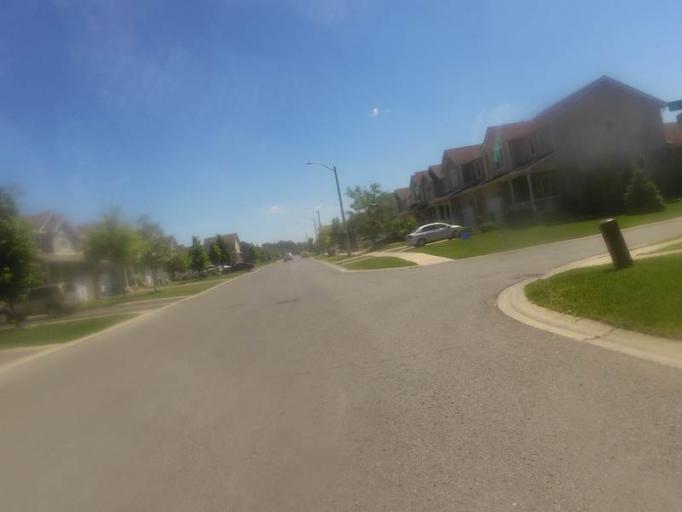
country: CA
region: Ontario
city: Kingston
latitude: 44.2674
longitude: -76.5585
